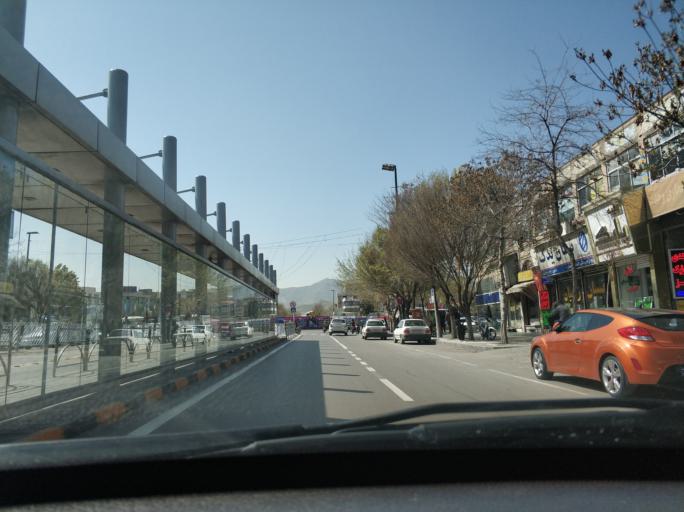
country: IR
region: Razavi Khorasan
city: Mashhad
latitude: 36.2692
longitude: 59.5995
